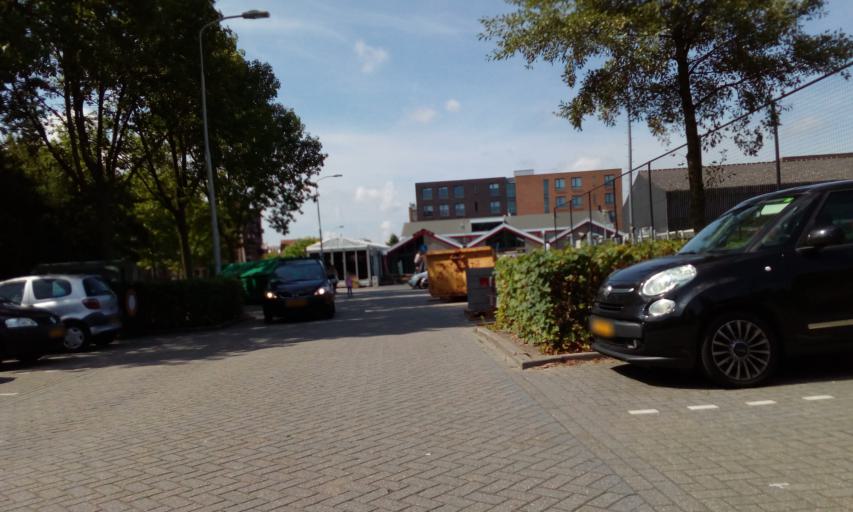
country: NL
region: South Holland
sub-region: Gemeente Den Haag
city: Ypenburg
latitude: 52.0472
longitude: 4.3930
